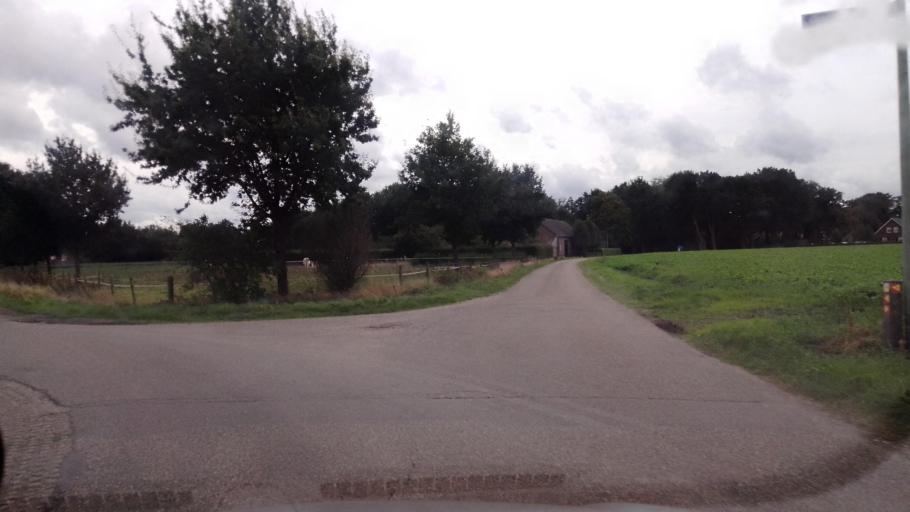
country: NL
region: Limburg
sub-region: Gemeente Peel en Maas
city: Maasbree
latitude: 51.4193
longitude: 6.0508
